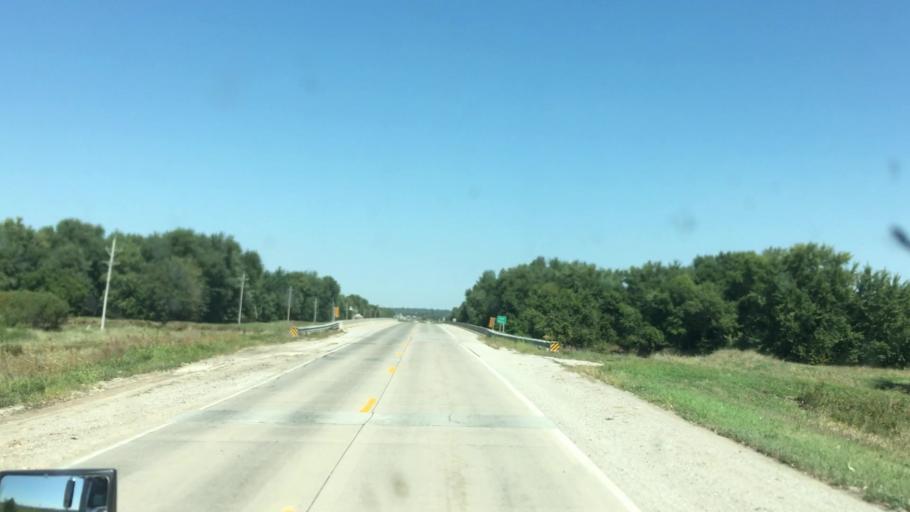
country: US
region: Iowa
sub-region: Benton County
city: Belle Plaine
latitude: 41.8580
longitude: -92.2780
